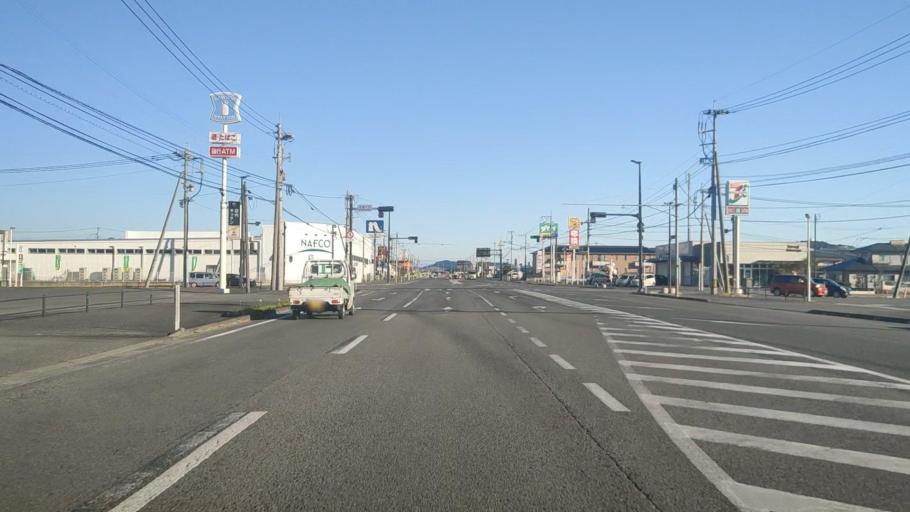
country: JP
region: Miyazaki
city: Nobeoka
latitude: 32.3962
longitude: 131.6292
